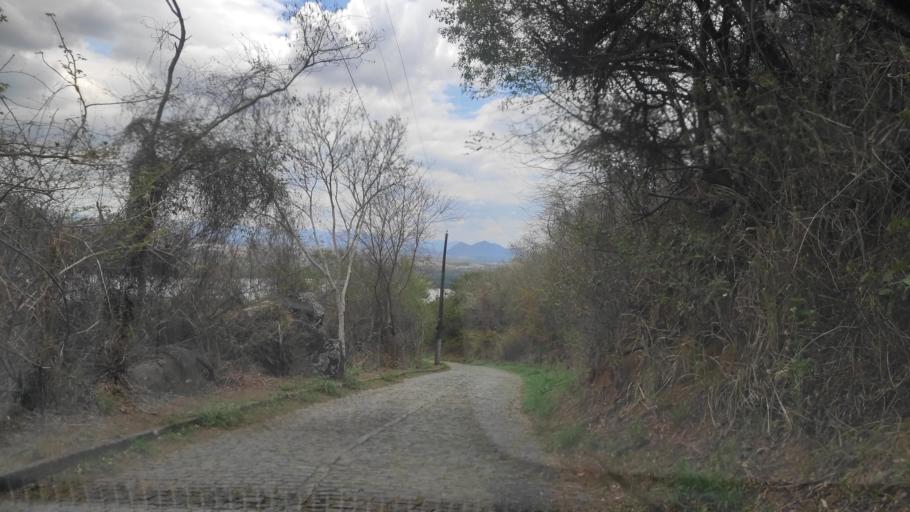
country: BR
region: Espirito Santo
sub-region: Vitoria
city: Vitoria
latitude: -20.2946
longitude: -40.3370
